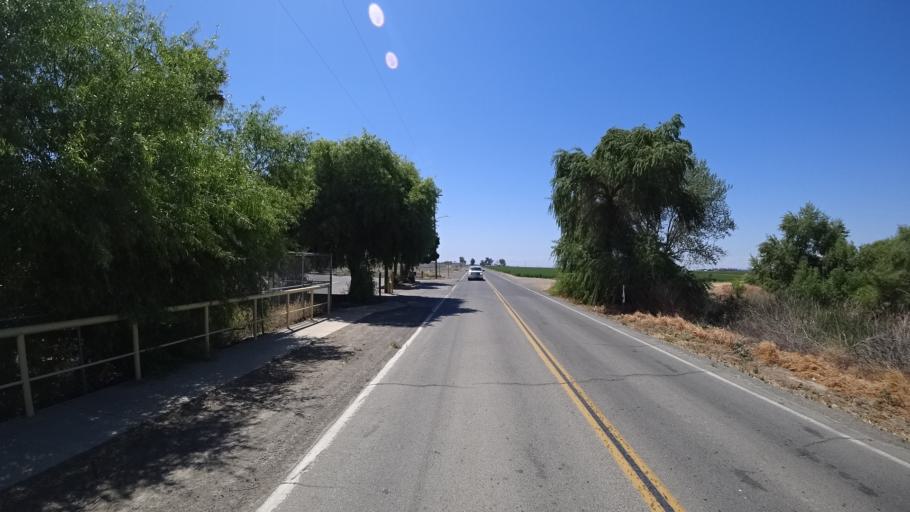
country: US
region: California
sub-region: Kings County
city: Lemoore
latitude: 36.2332
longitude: -119.7627
